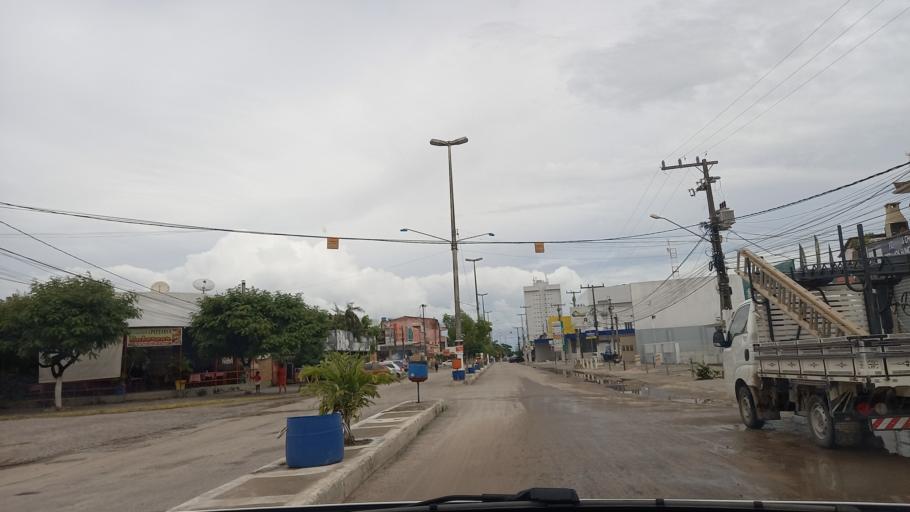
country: BR
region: Pernambuco
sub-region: Sao Jose Da Coroa Grande
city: Sao Jose da Coroa Grande
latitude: -8.8959
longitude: -35.1487
